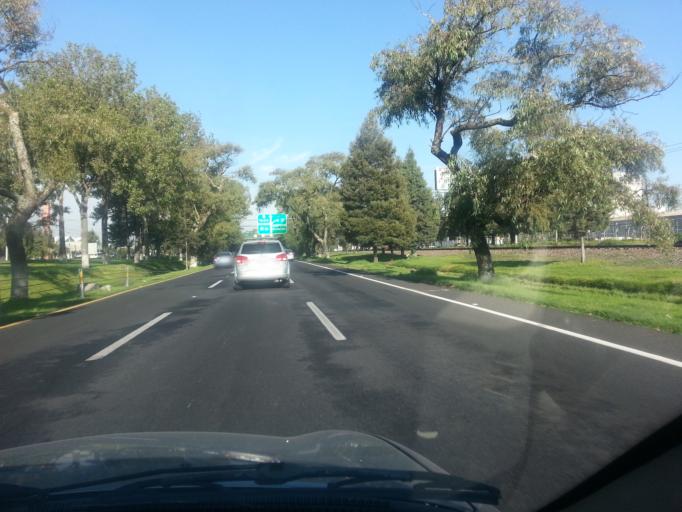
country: MX
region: Mexico
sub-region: San Mateo Atenco
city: Santa Maria la Asuncion
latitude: 19.2862
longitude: -99.5469
